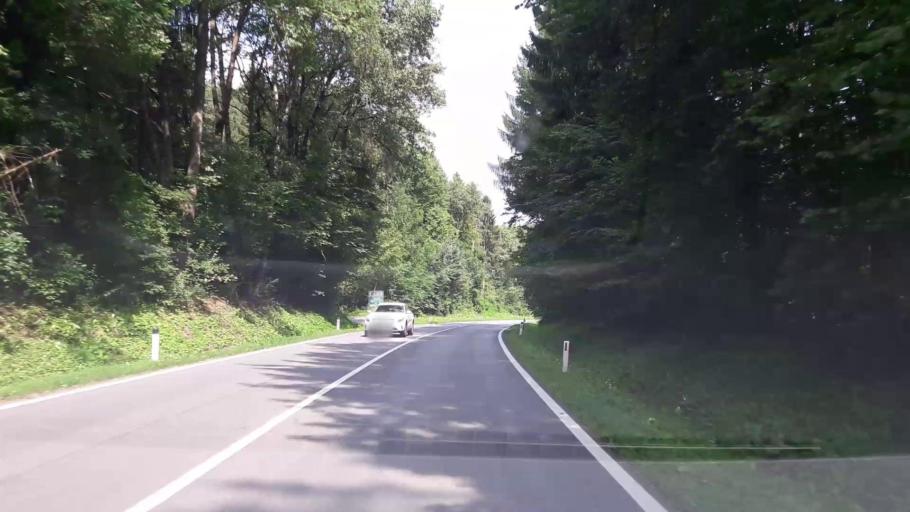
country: AT
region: Styria
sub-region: Politischer Bezirk Hartberg-Fuerstenfeld
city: Kaindorf
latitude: 47.2453
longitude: 15.9301
